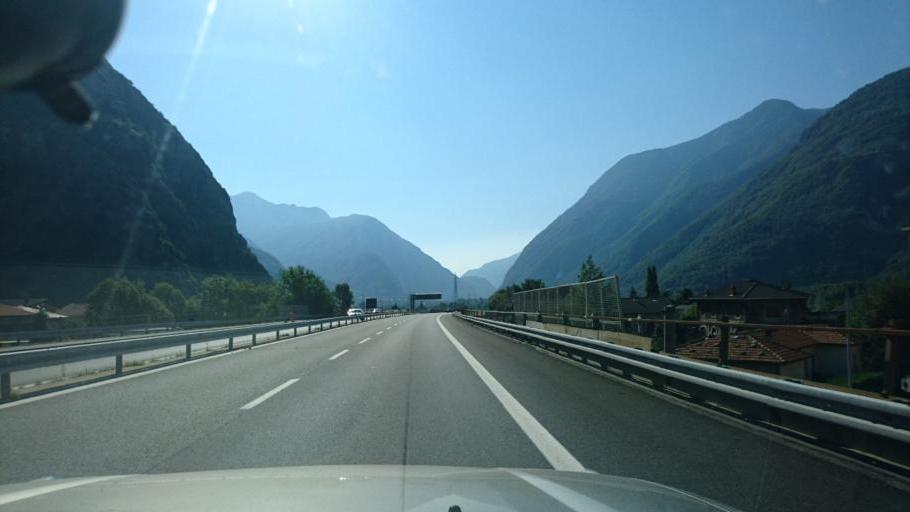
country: IT
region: Aosta Valley
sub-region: Valle d'Aosta
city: Verres
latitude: 45.6612
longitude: 7.6906
